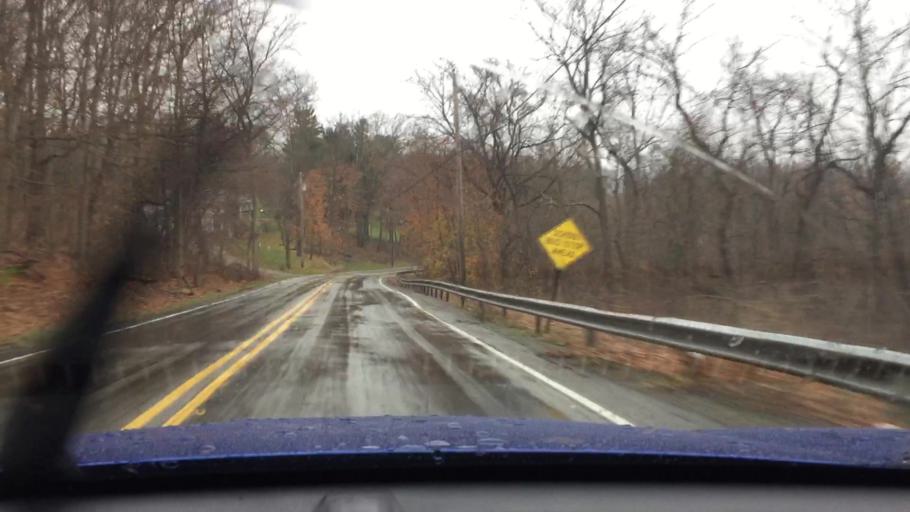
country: US
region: Pennsylvania
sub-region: Washington County
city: McMurray
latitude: 40.1931
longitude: -80.1113
